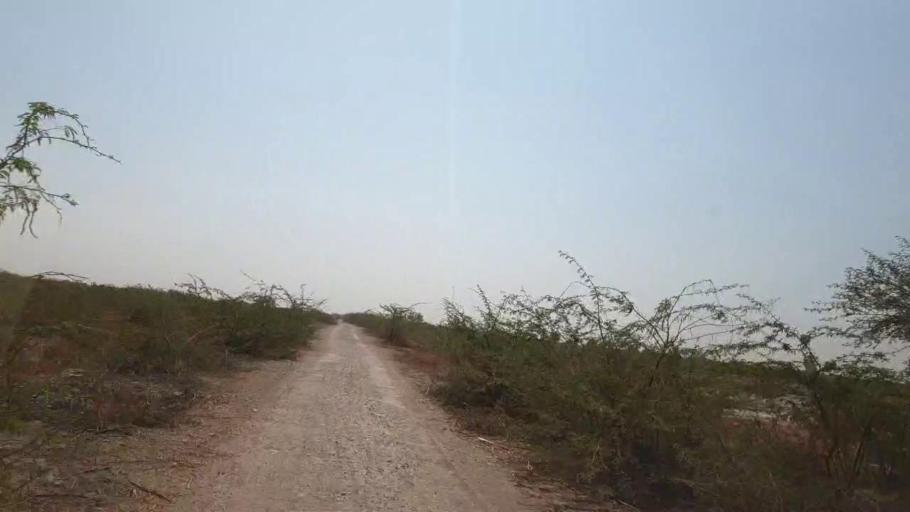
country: PK
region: Sindh
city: Kunri
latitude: 25.0926
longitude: 69.4742
